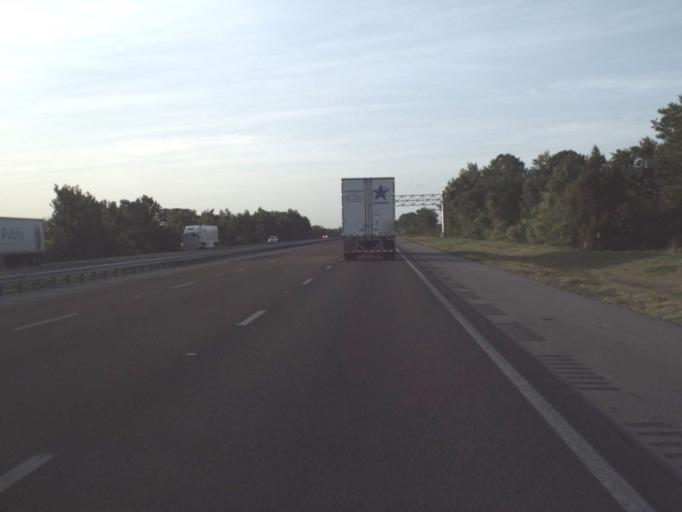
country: US
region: Florida
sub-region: Brevard County
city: Mims
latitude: 28.7516
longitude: -80.8882
